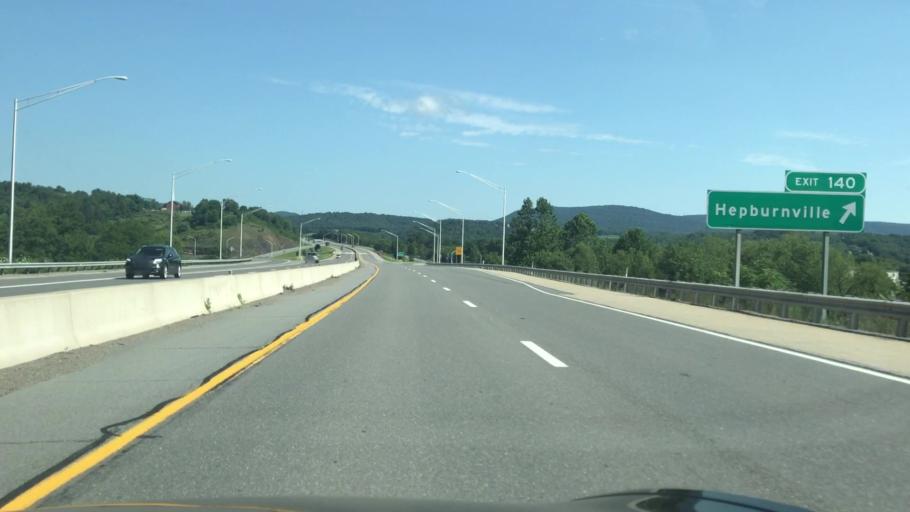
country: US
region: Pennsylvania
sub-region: Lycoming County
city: Garden View
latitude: 41.2875
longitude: -77.0642
